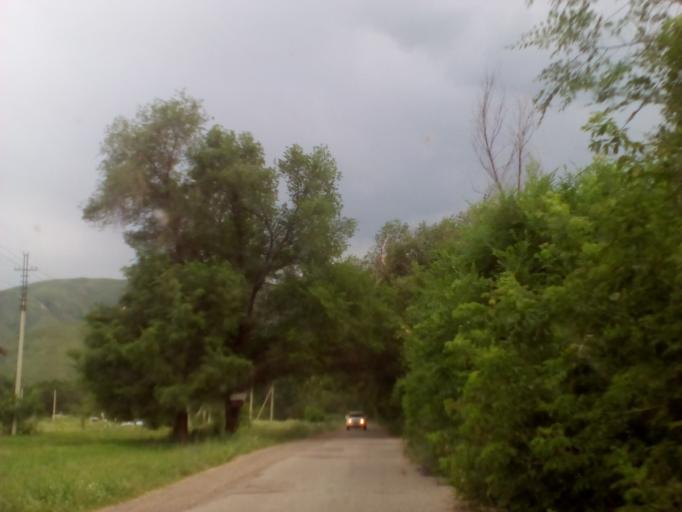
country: KZ
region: Almaty Oblysy
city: Burunday
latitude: 43.1613
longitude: 76.3875
